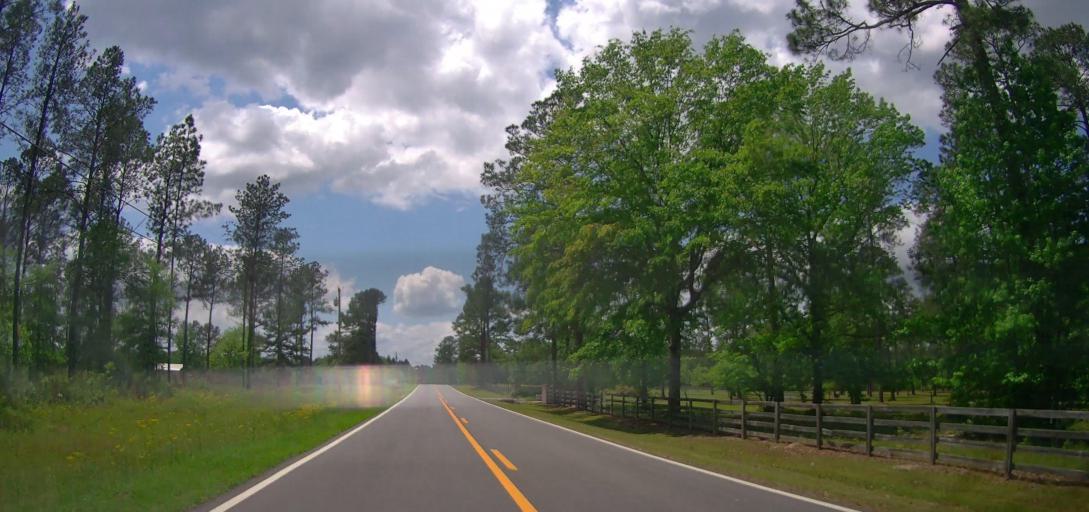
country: US
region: Georgia
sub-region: Laurens County
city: East Dublin
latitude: 32.6050
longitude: -82.8999
